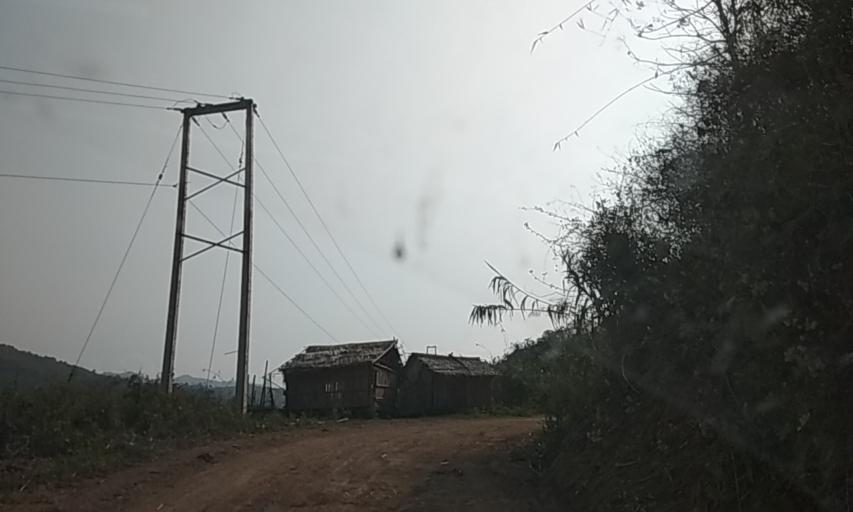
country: LA
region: Louangphabang
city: Louangphabang
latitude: 20.0430
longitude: 101.8364
